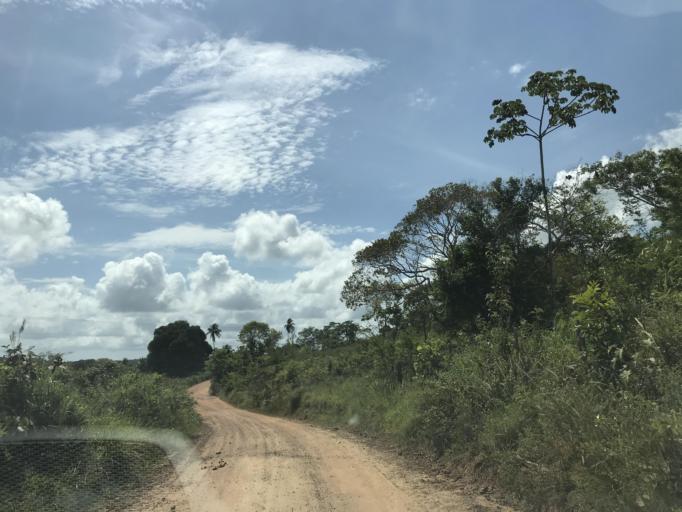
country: BR
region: Bahia
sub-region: Entre Rios
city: Entre Rios
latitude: -12.1798
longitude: -38.0601
